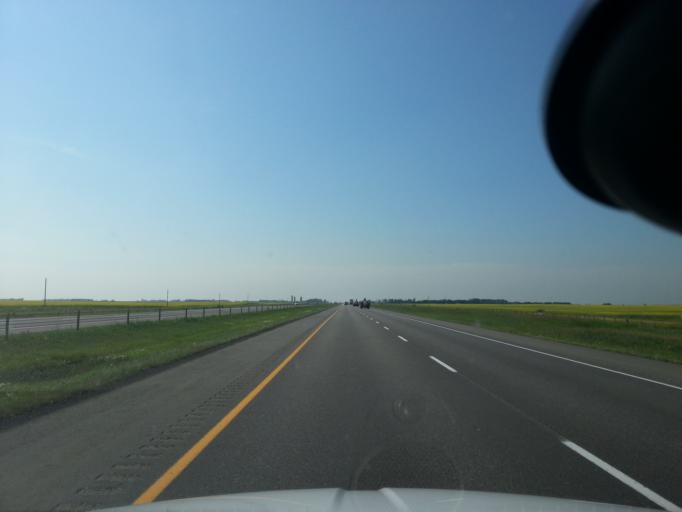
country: CA
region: Alberta
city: Olds
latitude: 51.7452
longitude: -114.0256
